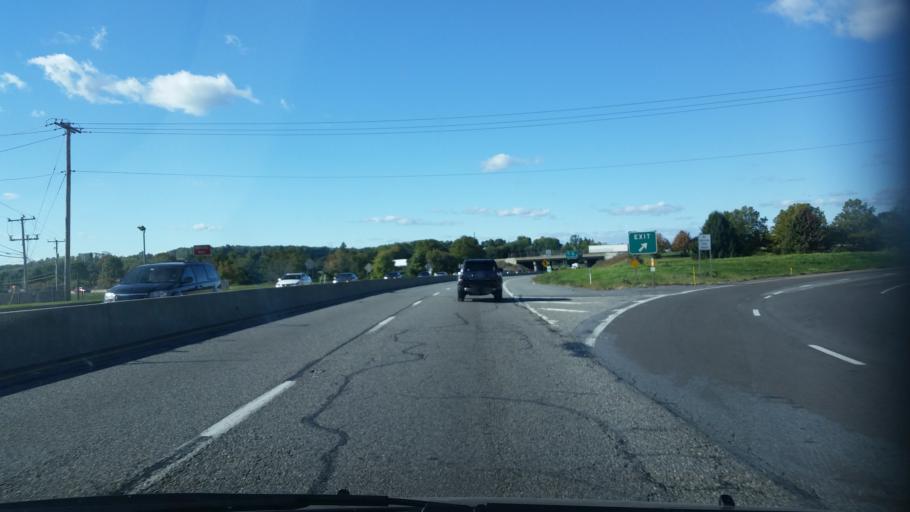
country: US
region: Pennsylvania
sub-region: Lehigh County
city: Trexlertown
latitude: 40.5773
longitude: -75.6224
